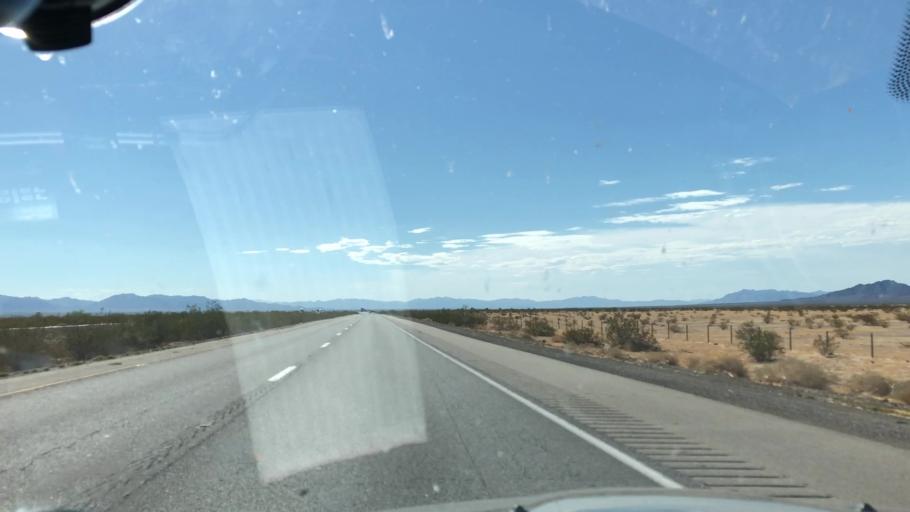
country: US
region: California
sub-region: Riverside County
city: Mesa Verde
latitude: 33.6184
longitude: -115.0268
